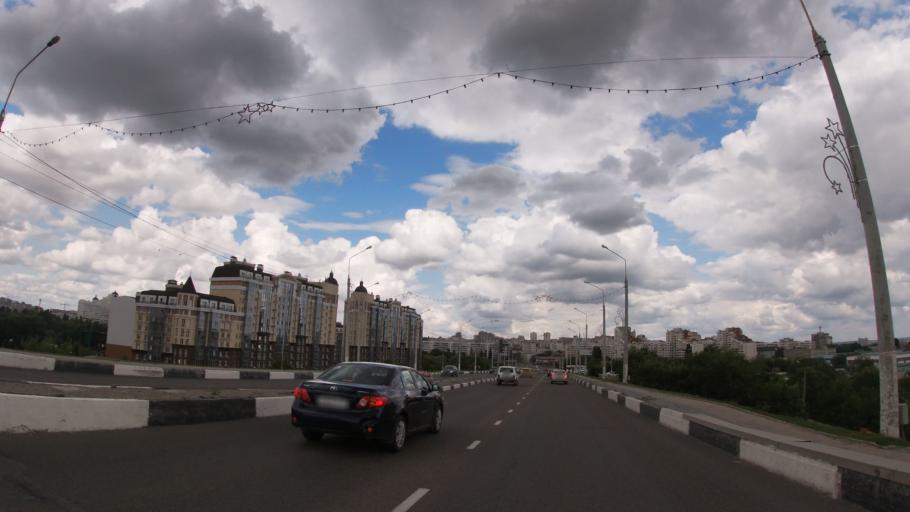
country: RU
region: Belgorod
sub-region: Belgorodskiy Rayon
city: Belgorod
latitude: 50.5870
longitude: 36.5878
